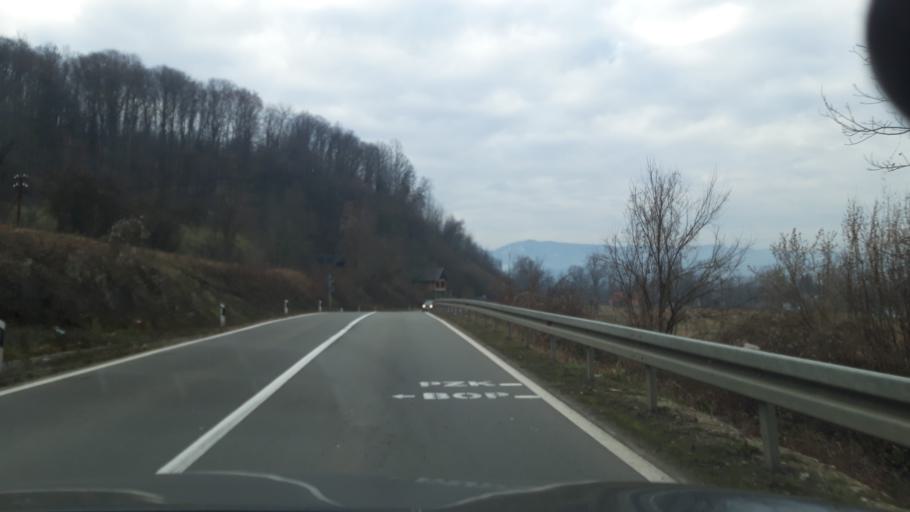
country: BA
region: Republika Srpska
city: Zvornik
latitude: 44.4256
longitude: 19.1504
